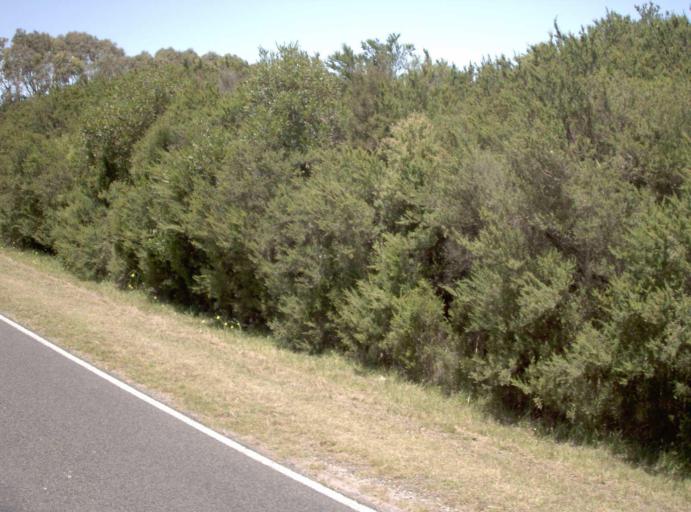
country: AU
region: Victoria
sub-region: Latrobe
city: Morwell
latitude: -38.7872
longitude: 146.1717
